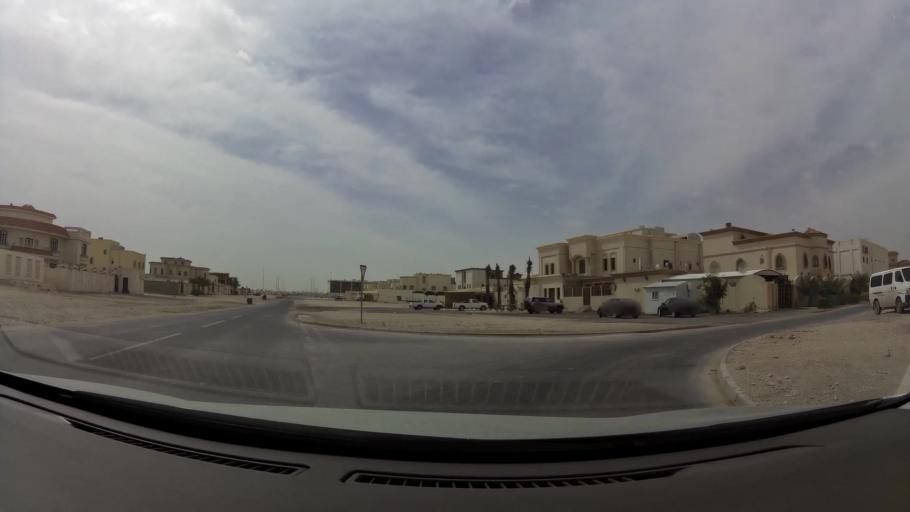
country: QA
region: Al Wakrah
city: Al Wukayr
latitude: 25.2003
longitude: 51.4606
